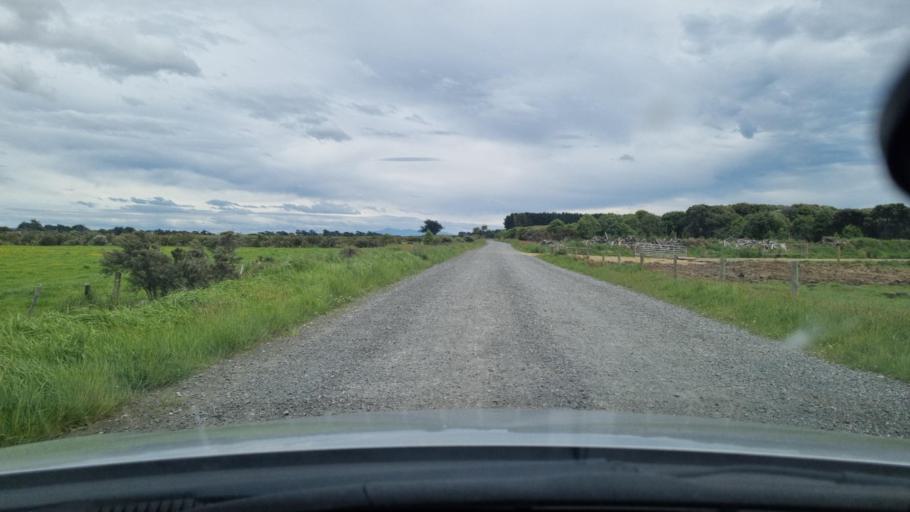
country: NZ
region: Southland
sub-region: Invercargill City
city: Invercargill
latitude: -46.4037
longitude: 168.2802
